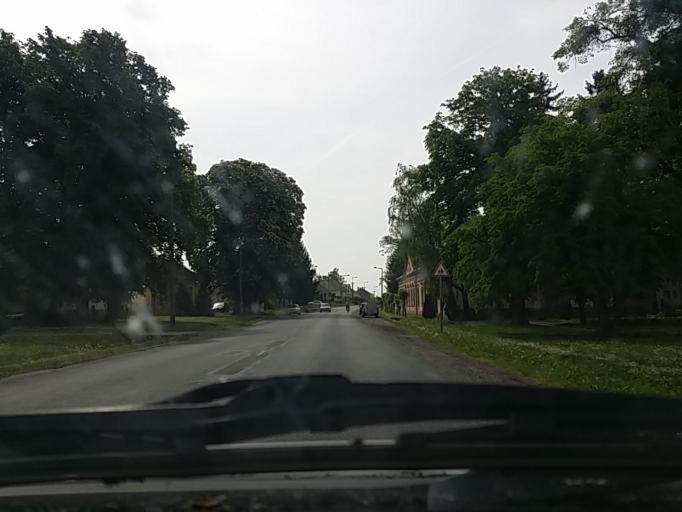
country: HU
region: Somogy
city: Csurgo
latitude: 46.2525
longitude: 17.1015
